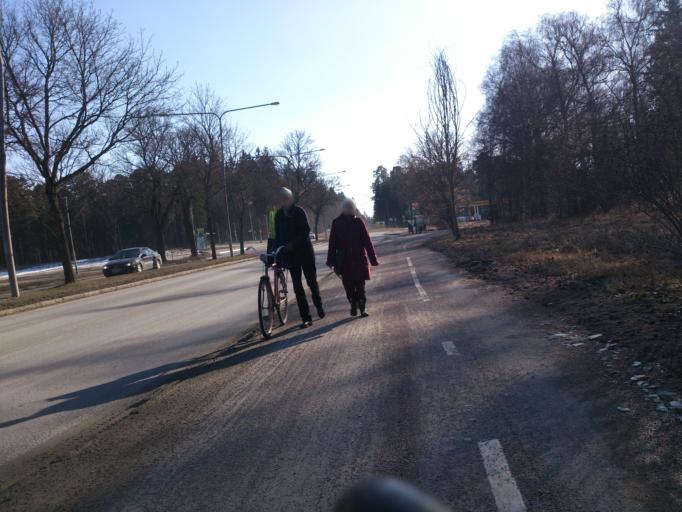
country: SE
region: Uppsala
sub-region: Uppsala Kommun
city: Uppsala
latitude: 59.8409
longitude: 17.6392
